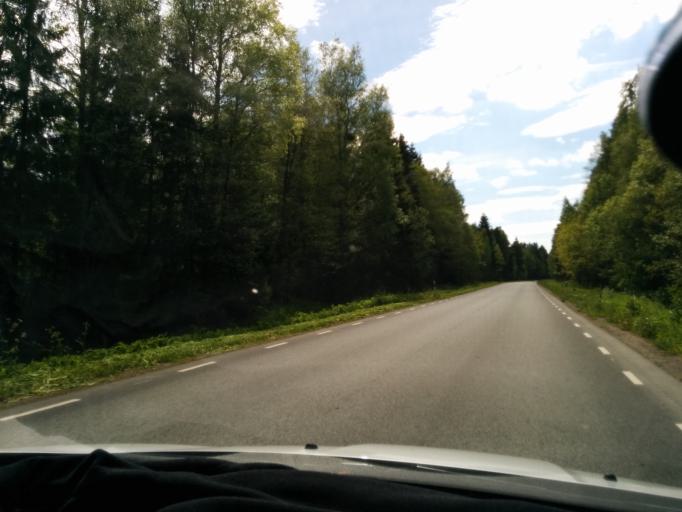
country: EE
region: Harju
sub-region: Loksa linn
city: Loksa
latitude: 59.5473
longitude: 25.7687
